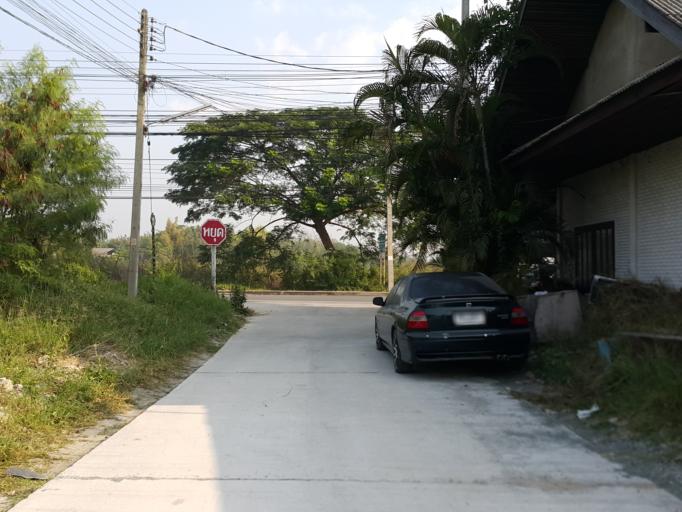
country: TH
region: Chiang Mai
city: San Kamphaeng
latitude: 18.7515
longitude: 99.1064
